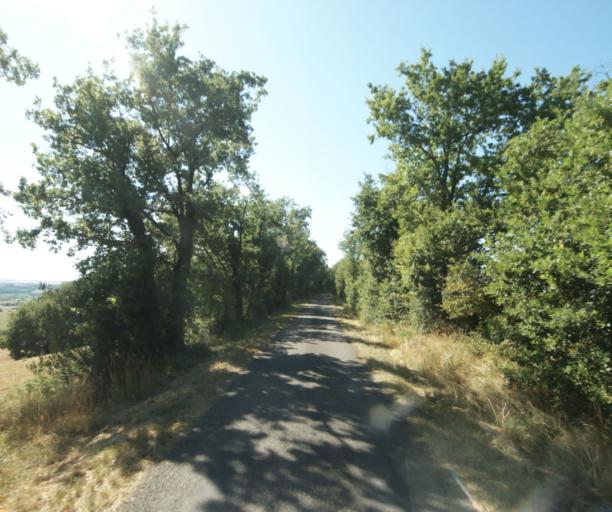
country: FR
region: Midi-Pyrenees
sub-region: Departement de la Haute-Garonne
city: Saint-Felix-Lauragais
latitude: 43.5211
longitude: 1.9121
